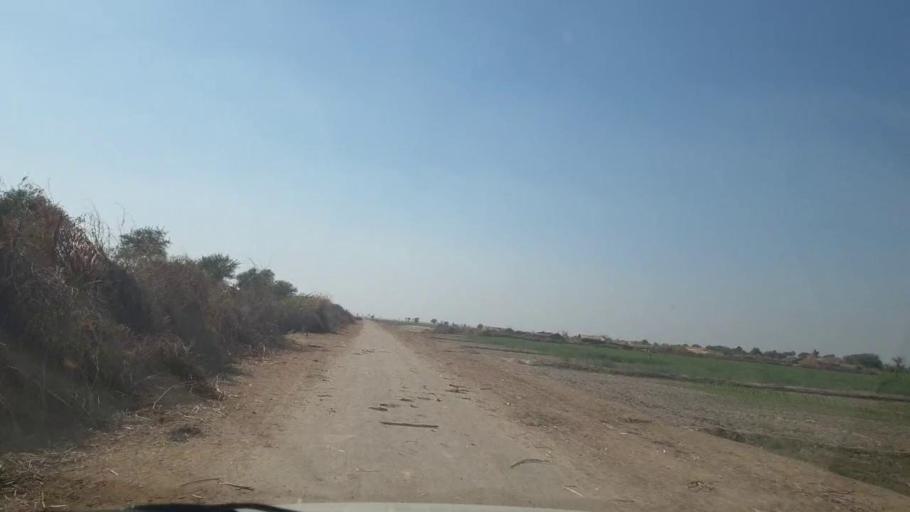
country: PK
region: Sindh
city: Mirpur Khas
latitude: 25.4709
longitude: 69.1735
